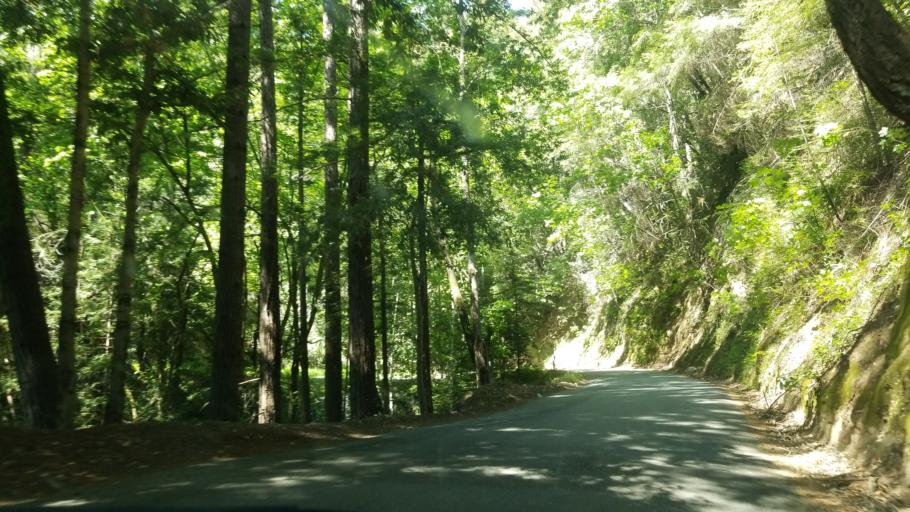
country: US
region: California
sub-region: Santa Cruz County
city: Day Valley
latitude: 37.0574
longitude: -121.8186
